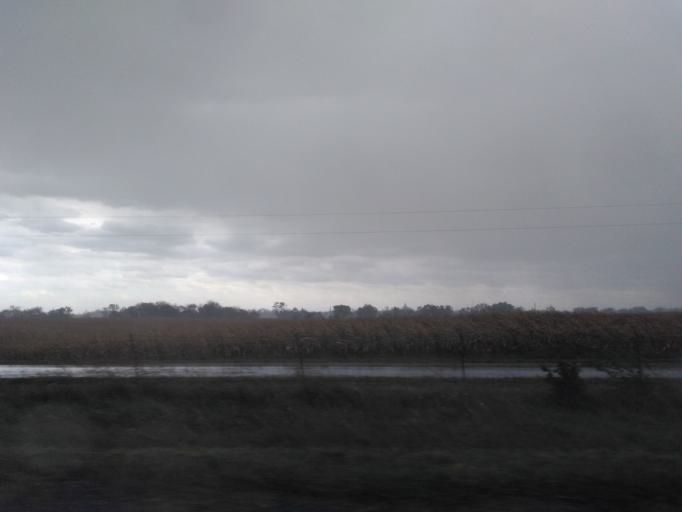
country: US
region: Illinois
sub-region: Madison County
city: Highland
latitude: 38.7966
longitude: -89.6082
